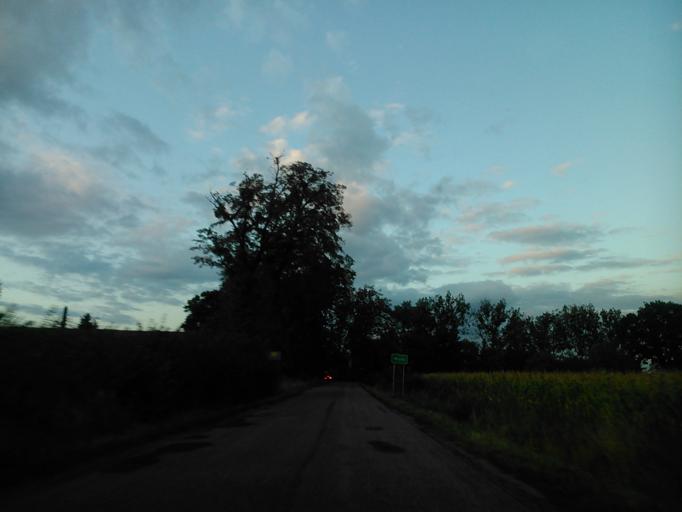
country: PL
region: Kujawsko-Pomorskie
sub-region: Powiat wabrzeski
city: Debowa Laka
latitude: 53.2020
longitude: 19.1649
